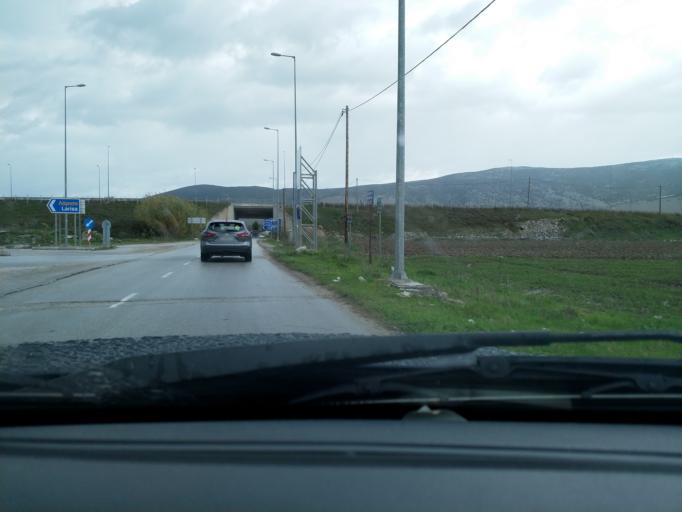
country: GR
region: Thessaly
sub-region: Trikala
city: Taxiarches
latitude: 39.5613
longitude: 21.8894
